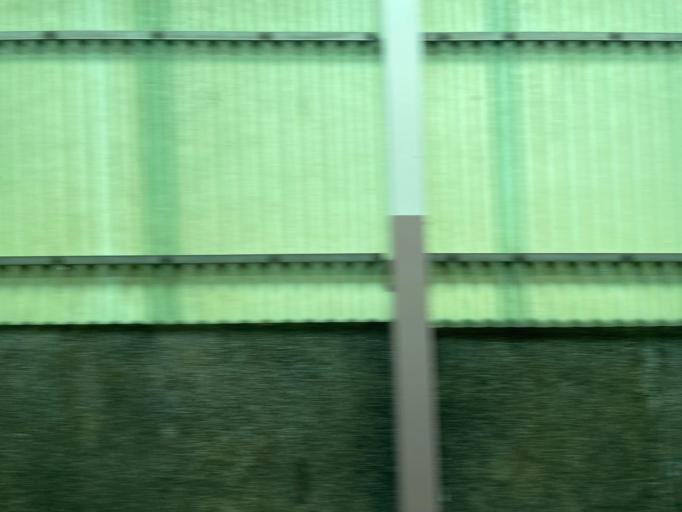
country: JP
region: Niigata
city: Shiozawa
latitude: 36.9895
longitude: 138.8041
